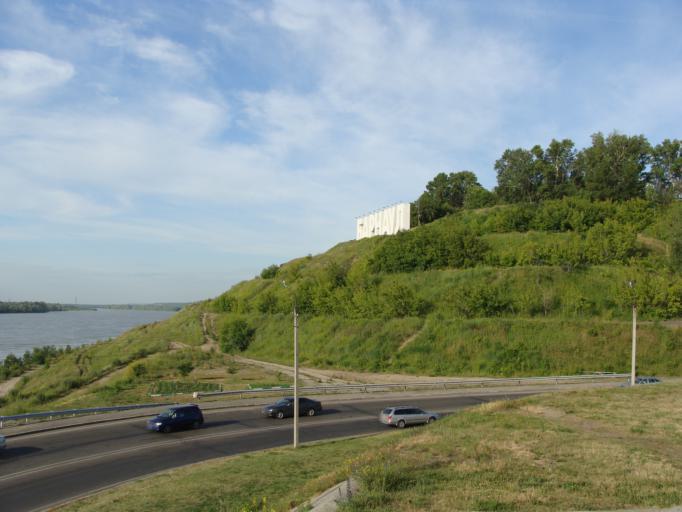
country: RU
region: Altai Krai
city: Zaton
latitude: 53.3246
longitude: 83.7987
